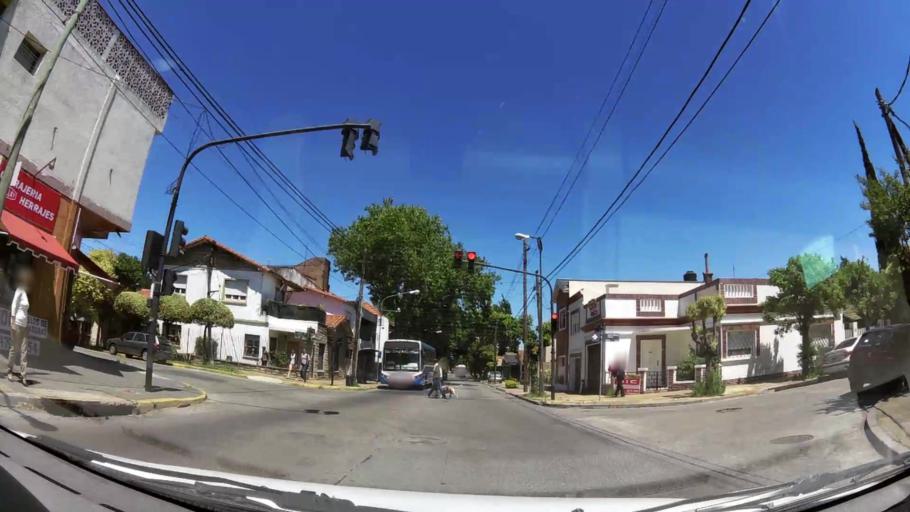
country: AR
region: Buenos Aires
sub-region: Partido de Vicente Lopez
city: Olivos
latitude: -34.4989
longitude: -58.5004
